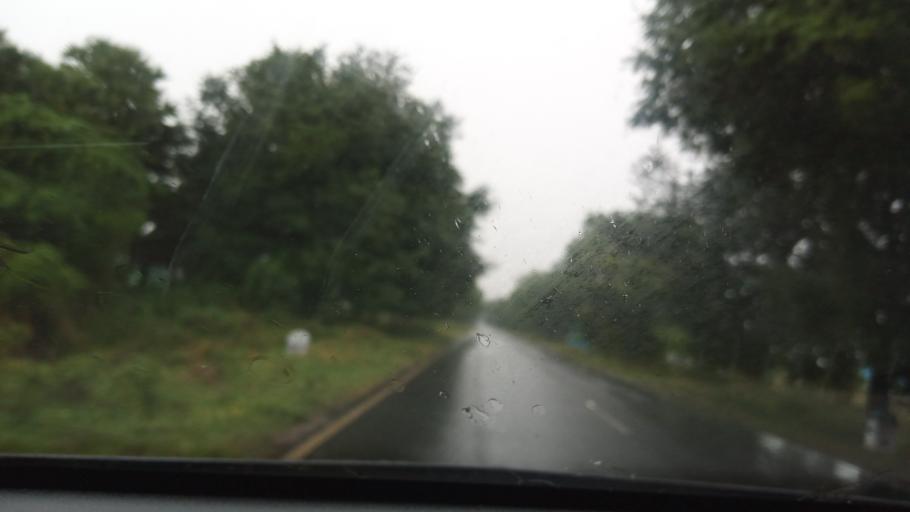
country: IN
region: Tamil Nadu
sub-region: Vellore
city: Kalavai
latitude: 12.8415
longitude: 79.4017
